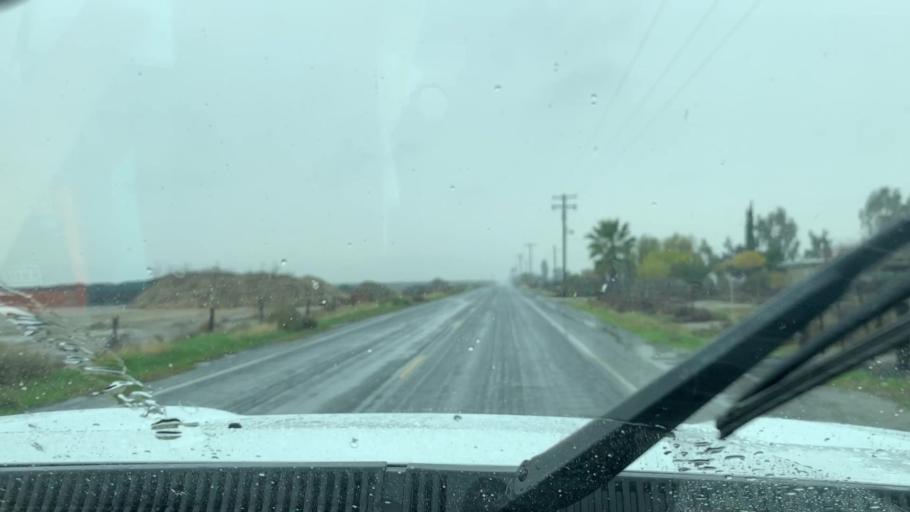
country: US
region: California
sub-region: Tulare County
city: Earlimart
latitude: 35.8919
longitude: -119.3133
